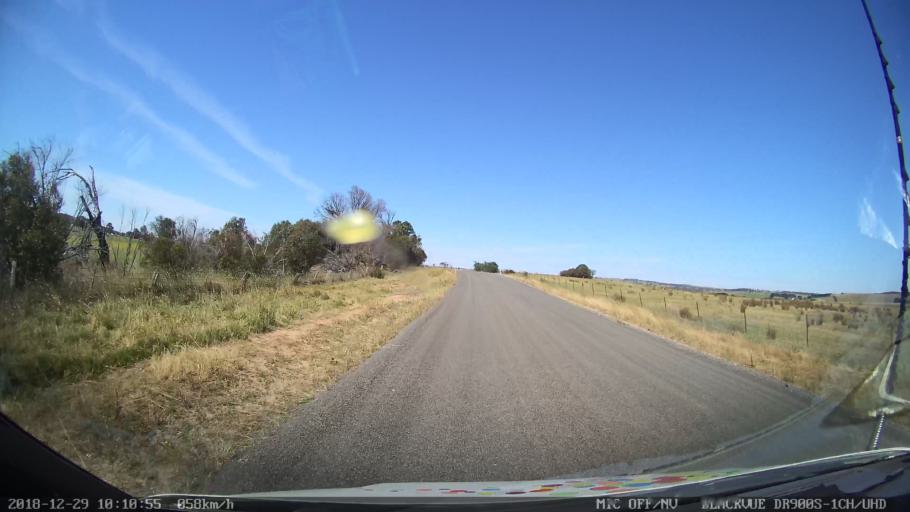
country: AU
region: New South Wales
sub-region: Yass Valley
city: Gundaroo
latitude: -34.8791
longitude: 149.4544
